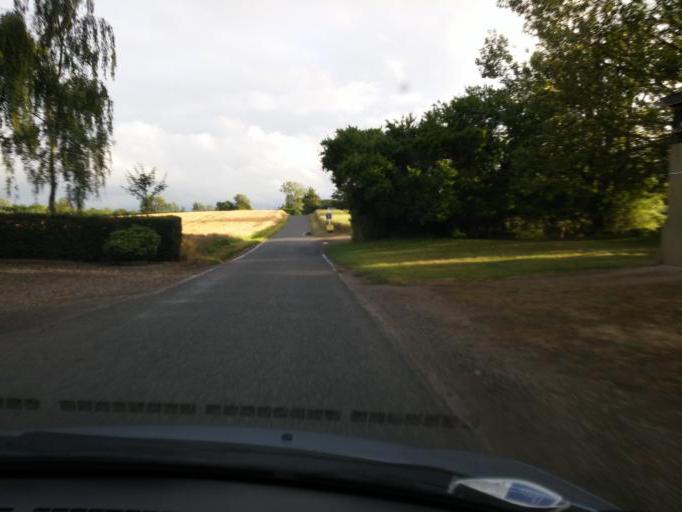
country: DK
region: South Denmark
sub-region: Kerteminde Kommune
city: Munkebo
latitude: 55.5198
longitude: 10.5761
